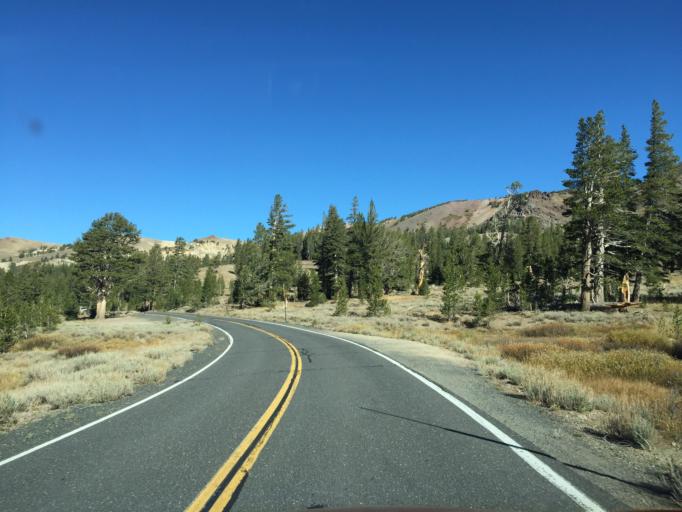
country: US
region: California
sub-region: Mono County
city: Bridgeport
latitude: 38.3344
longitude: -119.6415
